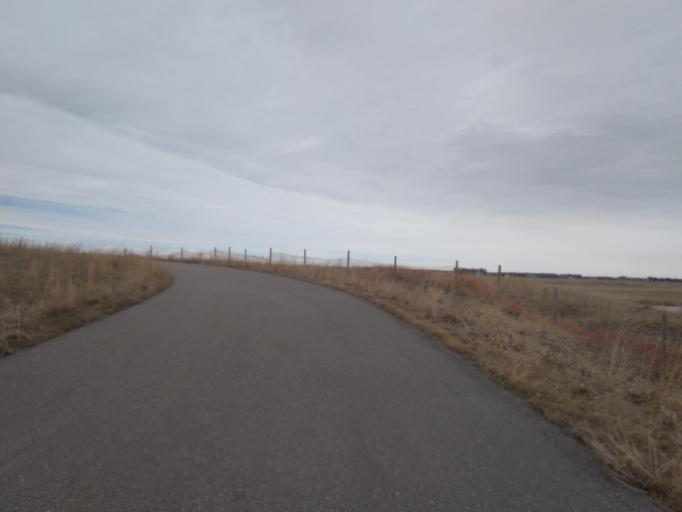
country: CA
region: Alberta
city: Calgary
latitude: 51.1442
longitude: -113.9537
